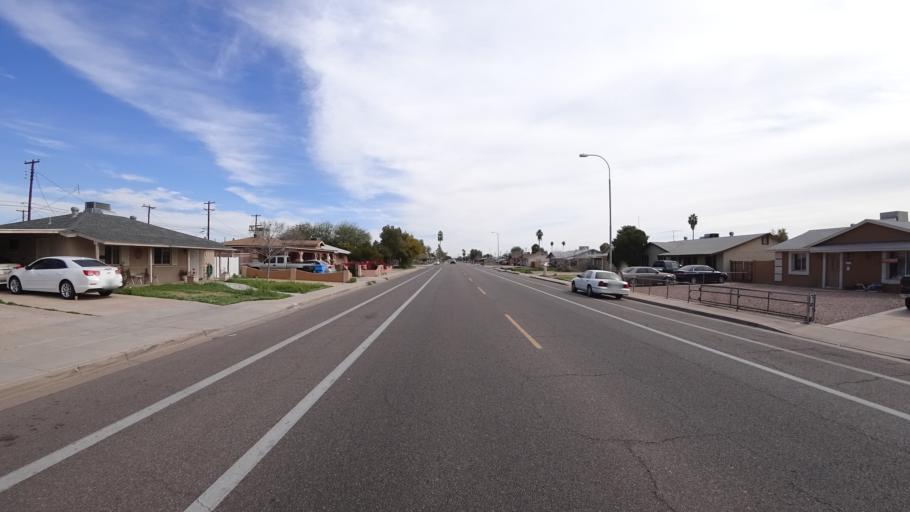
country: US
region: Arizona
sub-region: Maricopa County
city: Glendale
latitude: 33.4877
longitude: -112.1969
